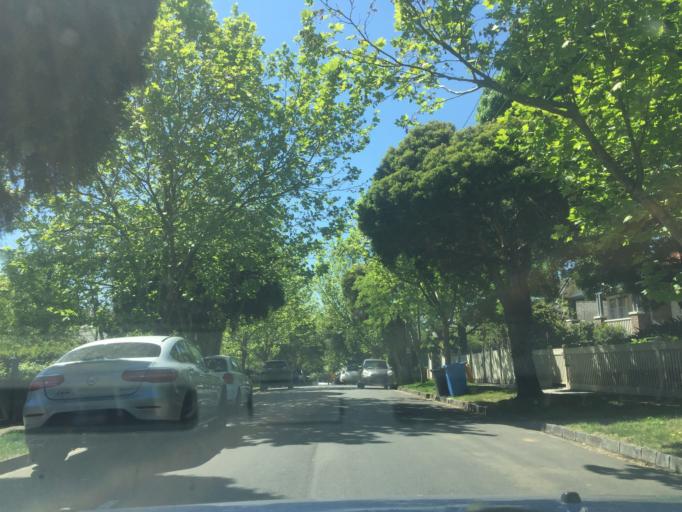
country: AU
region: Victoria
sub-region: Boroondara
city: Canterbury
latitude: -37.8261
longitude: 145.0852
